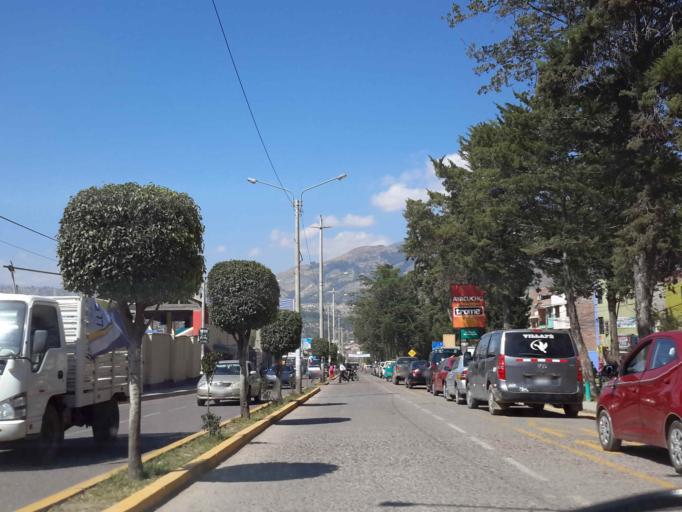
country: PE
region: Ayacucho
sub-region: Provincia de Huamanga
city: Ayacucho
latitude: -13.1513
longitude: -74.2231
